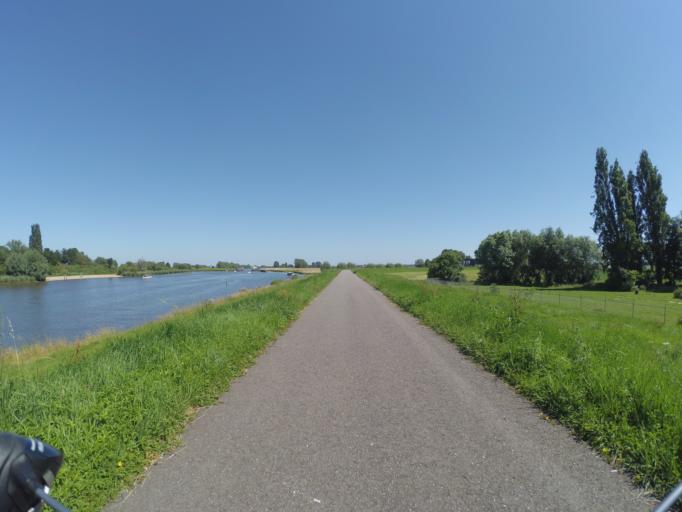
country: NL
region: North Brabant
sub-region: Gemeente Geertruidenberg
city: Geertruidenberg
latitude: 51.7137
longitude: 4.9028
